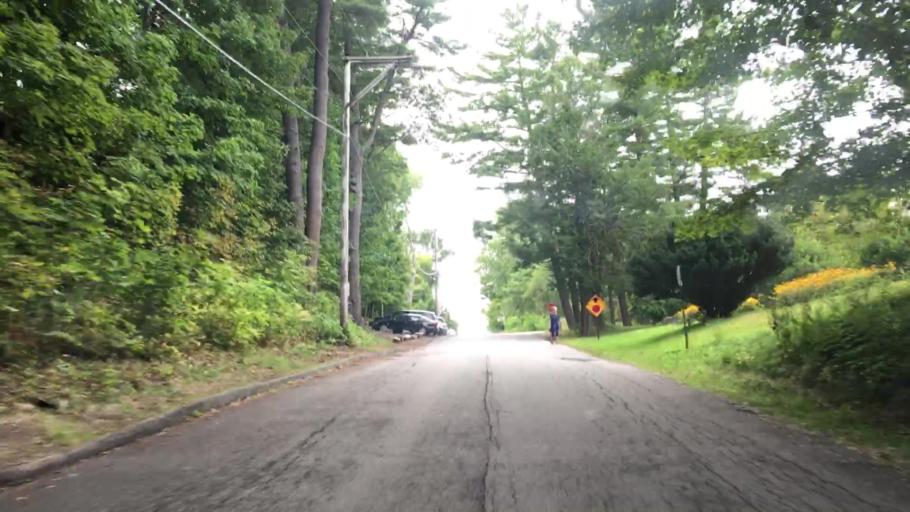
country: US
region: Maine
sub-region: Kennebec County
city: Hallowell
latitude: 44.2782
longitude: -69.7956
